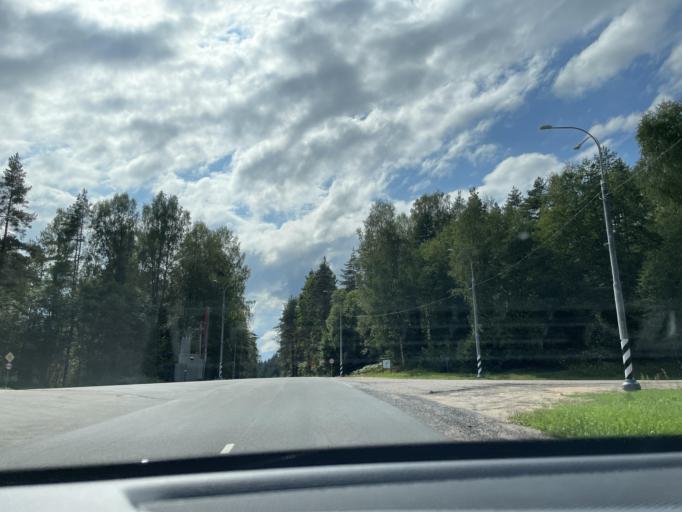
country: RU
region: Novgorod
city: Valday
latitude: 58.0281
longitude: 33.1992
